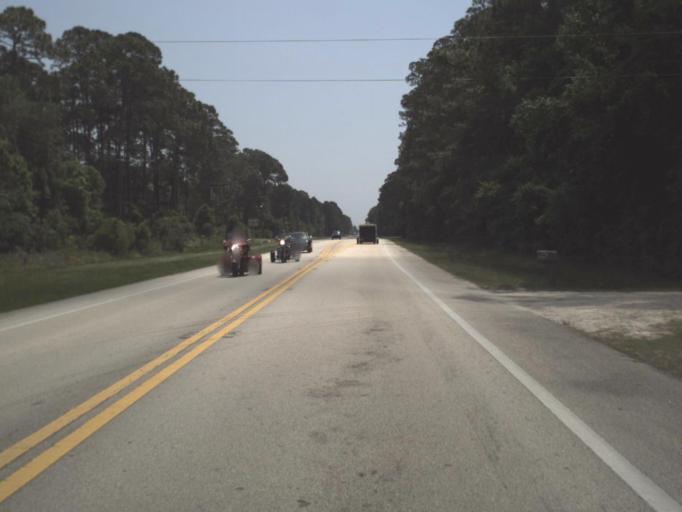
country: US
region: Florida
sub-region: Saint Johns County
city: Saint Augustine Shores
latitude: 29.7565
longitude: -81.3091
